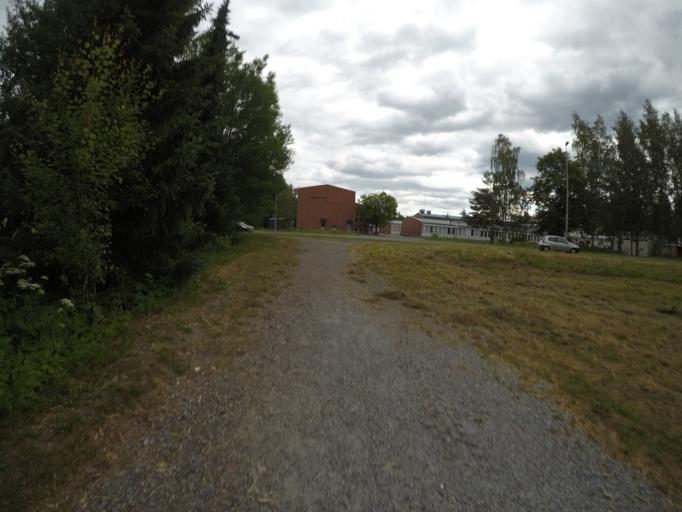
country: FI
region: Haeme
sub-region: Haemeenlinna
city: Haemeenlinna
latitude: 60.9893
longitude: 24.4318
